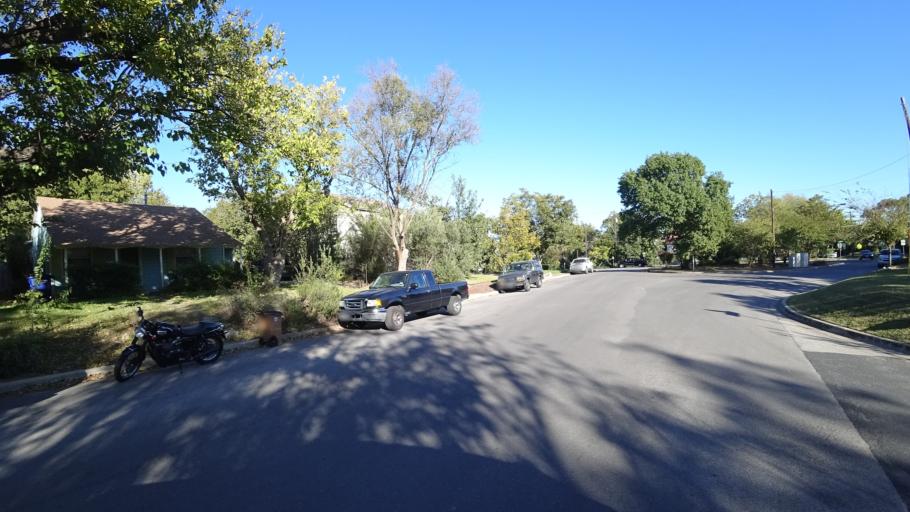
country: US
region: Texas
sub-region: Travis County
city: Austin
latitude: 30.3070
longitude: -97.7530
